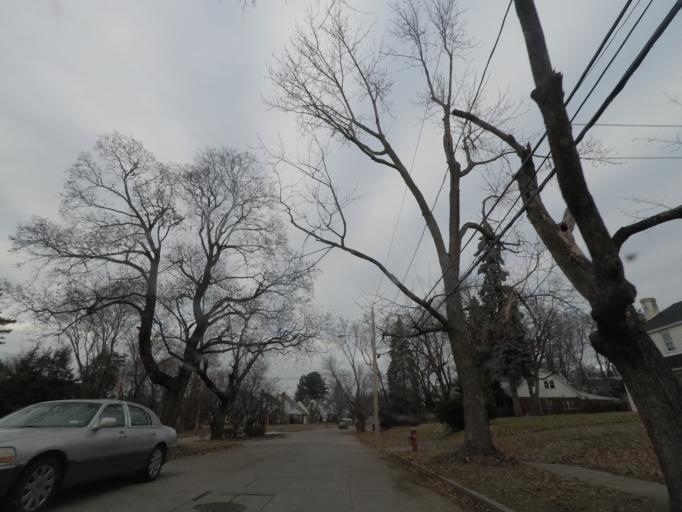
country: US
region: New York
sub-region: Albany County
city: Green Island
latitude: 42.7405
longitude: -73.6659
